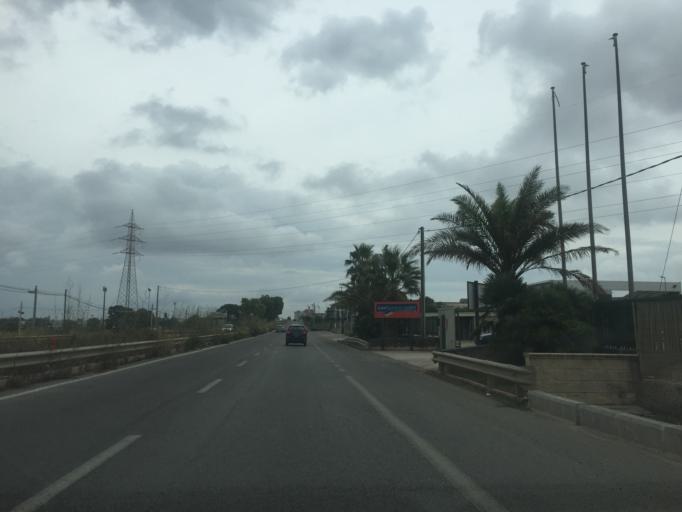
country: IT
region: Sicily
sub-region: Ragusa
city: Ragusa
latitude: 36.8831
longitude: 14.6813
